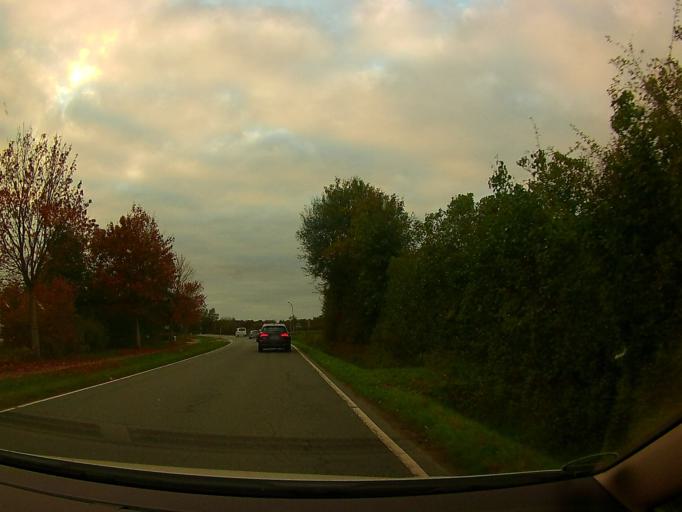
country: DE
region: Schleswig-Holstein
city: Breklum
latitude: 54.6099
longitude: 8.9893
